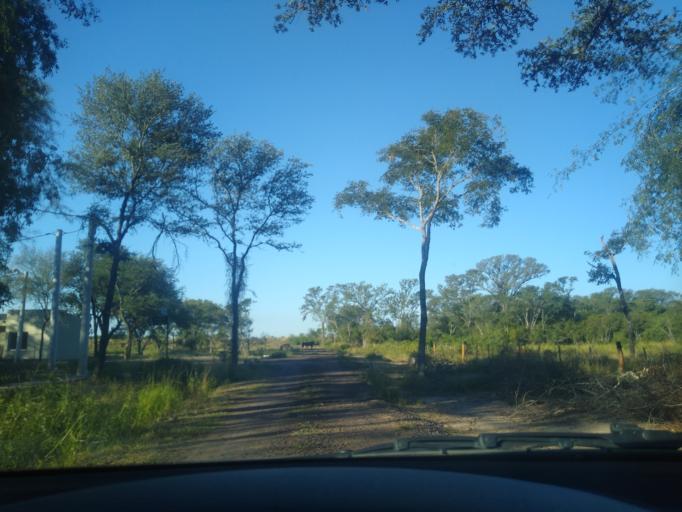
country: AR
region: Chaco
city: Resistencia
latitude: -27.4099
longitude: -58.9520
